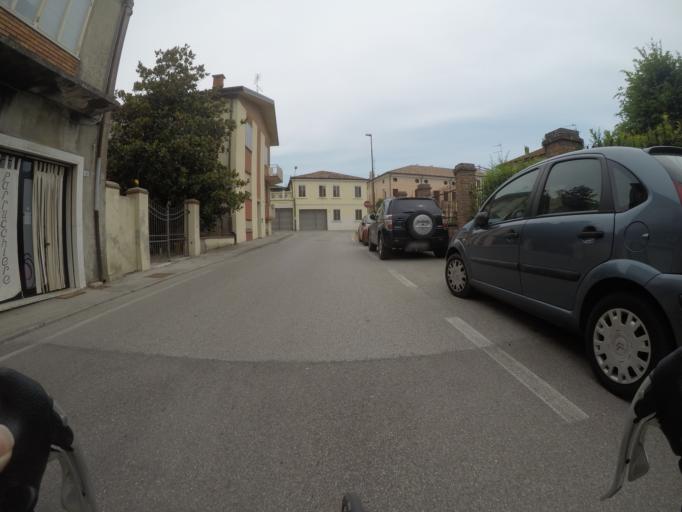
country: IT
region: Veneto
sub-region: Provincia di Rovigo
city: Costa di Rovigo
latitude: 45.0476
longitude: 11.6932
